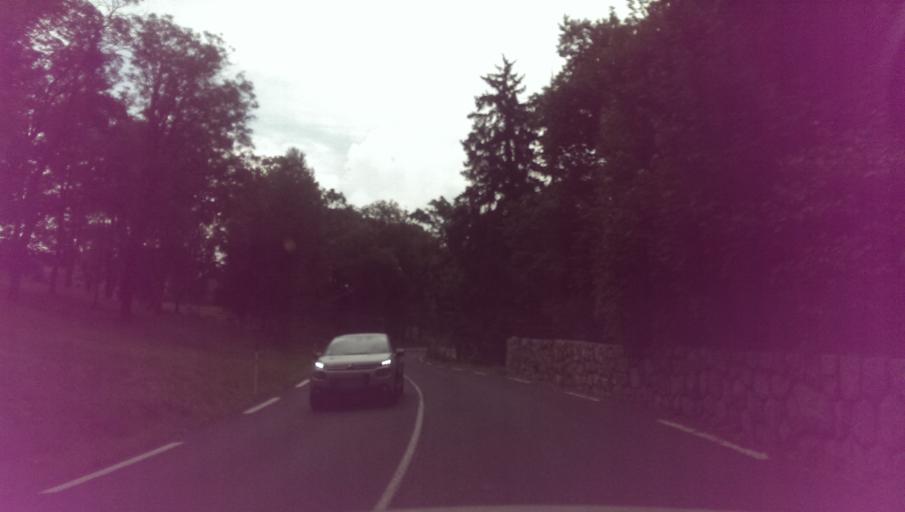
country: ES
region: Catalonia
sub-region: Provincia de Girona
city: Llivia
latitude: 42.5077
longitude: 2.1189
